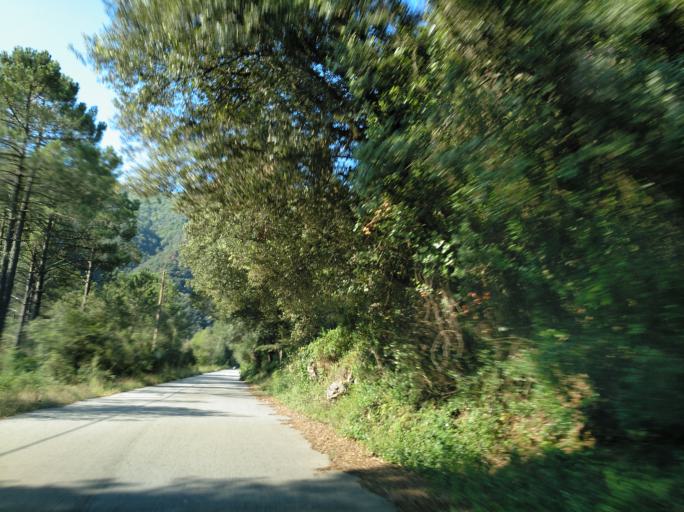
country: ES
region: Catalonia
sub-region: Provincia de Girona
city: Susqueda
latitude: 41.9883
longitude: 2.5544
